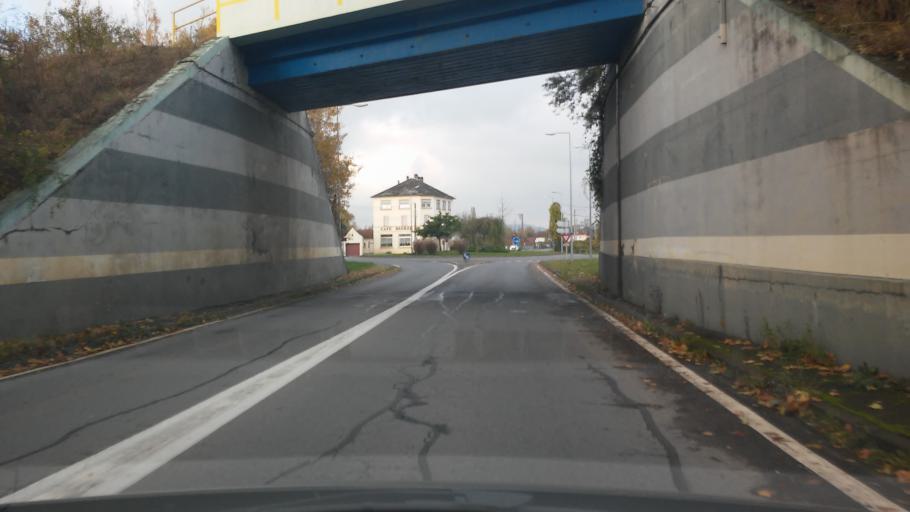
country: FR
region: Lorraine
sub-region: Departement de la Moselle
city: Uckange
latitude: 49.3264
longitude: 6.1531
